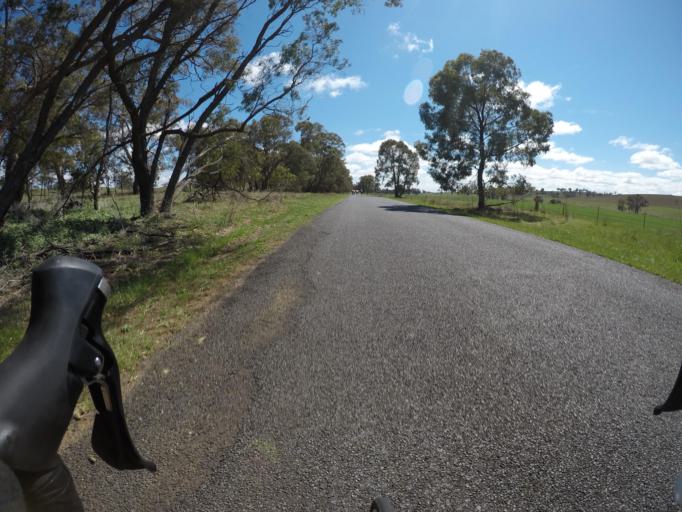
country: AU
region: New South Wales
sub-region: Dubbo Municipality
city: Dubbo
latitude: -32.5480
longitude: 148.5446
